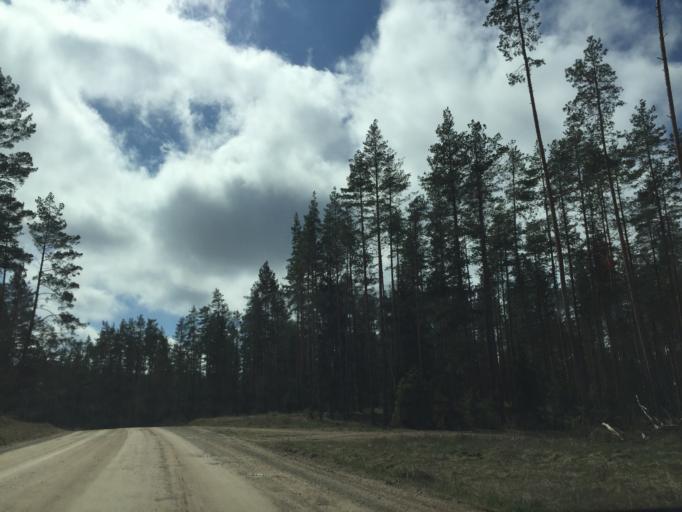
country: EE
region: Valgamaa
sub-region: Valga linn
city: Valga
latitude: 57.6295
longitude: 26.2343
